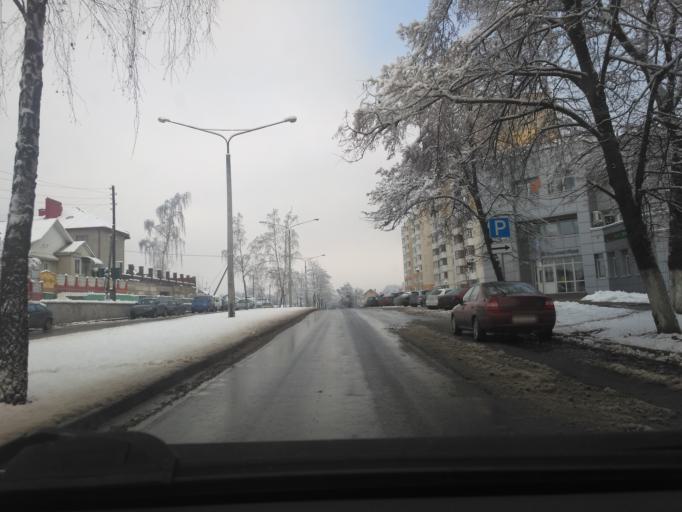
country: BY
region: Minsk
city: Horad Barysaw
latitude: 54.2246
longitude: 28.4986
